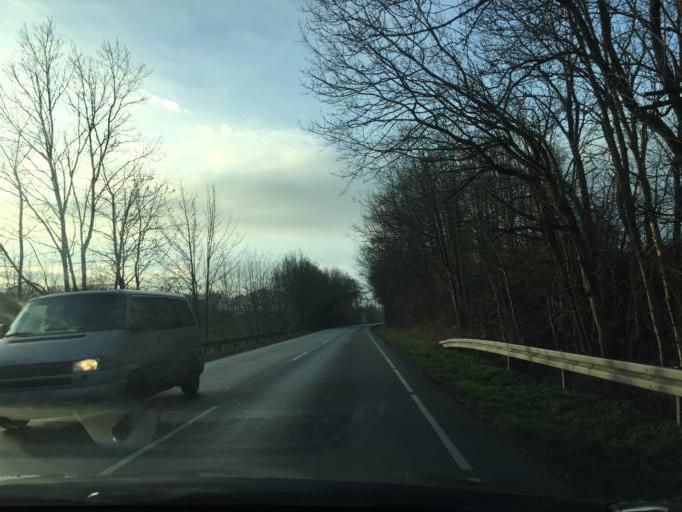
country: DK
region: South Denmark
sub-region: Faaborg-Midtfyn Kommune
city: Faaborg
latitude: 55.1635
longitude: 10.2755
